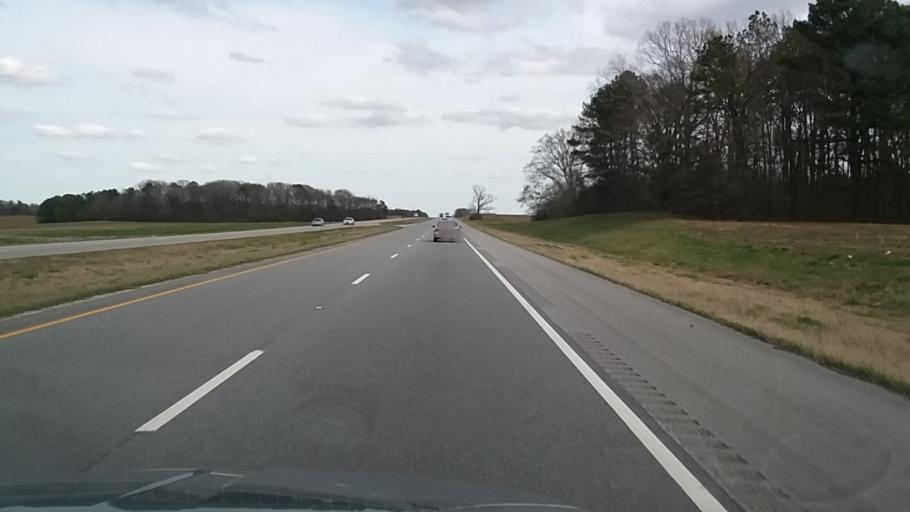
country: US
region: Alabama
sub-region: Lawrence County
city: Town Creek
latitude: 34.6828
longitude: -87.4822
